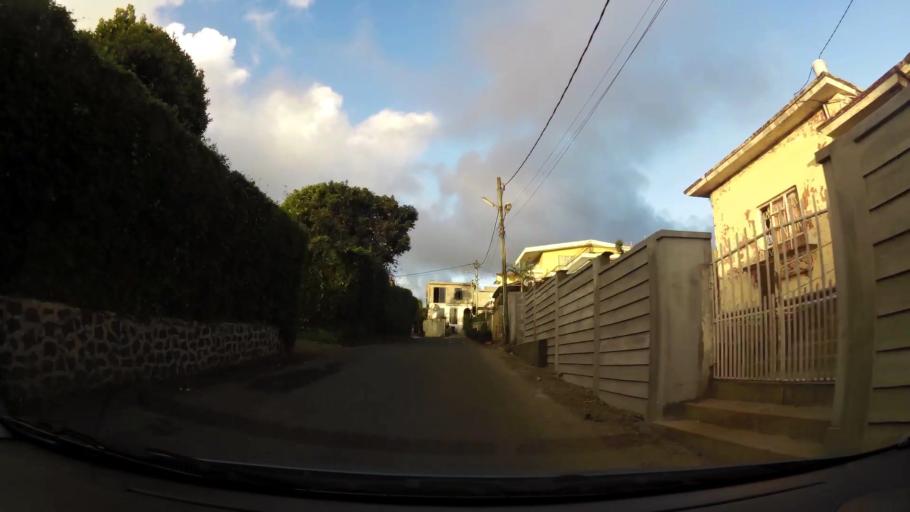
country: MU
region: Plaines Wilhems
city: Curepipe
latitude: -20.3095
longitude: 57.5302
